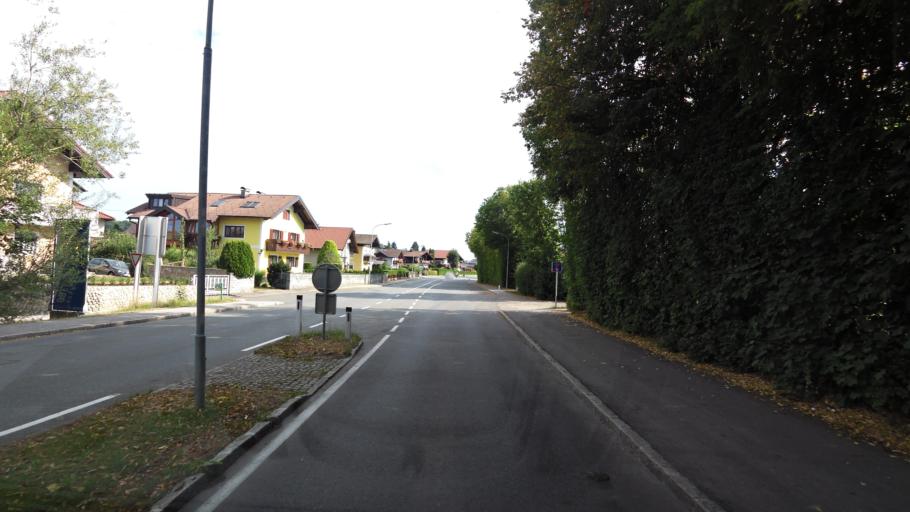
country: AT
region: Salzburg
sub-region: Politischer Bezirk Salzburg-Umgebung
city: Henndorf am Wallersee
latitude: 47.8929
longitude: 13.1807
